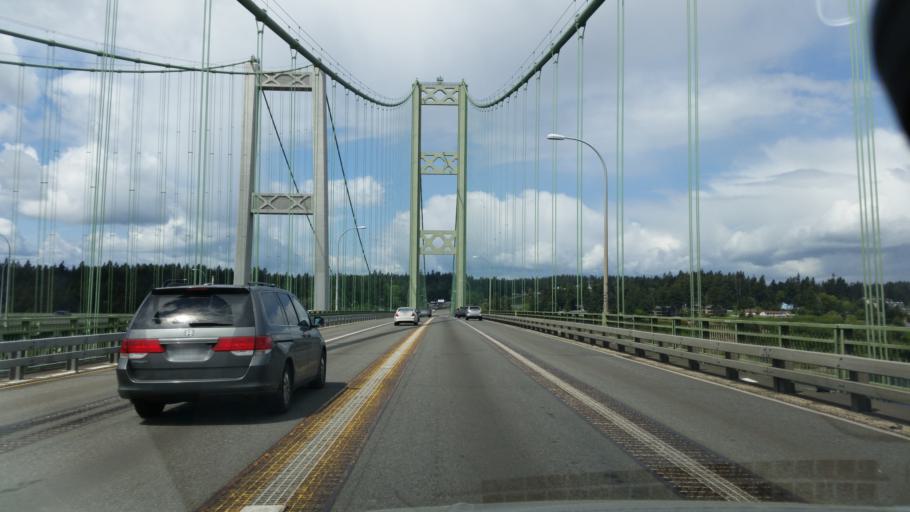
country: US
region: Washington
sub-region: Pierce County
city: Wollochet
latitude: 47.2692
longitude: -122.5515
